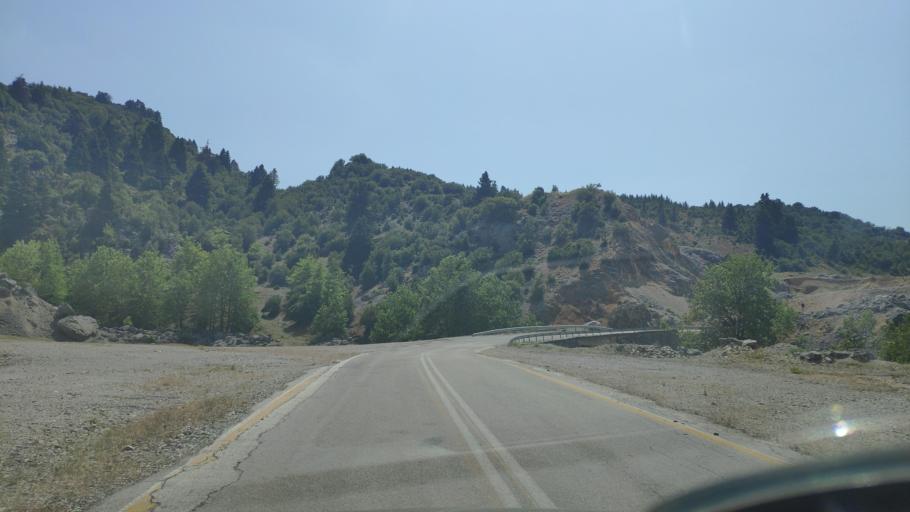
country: GR
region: Epirus
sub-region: Nomos Artas
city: Ano Kalentini
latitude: 39.2506
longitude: 21.2434
